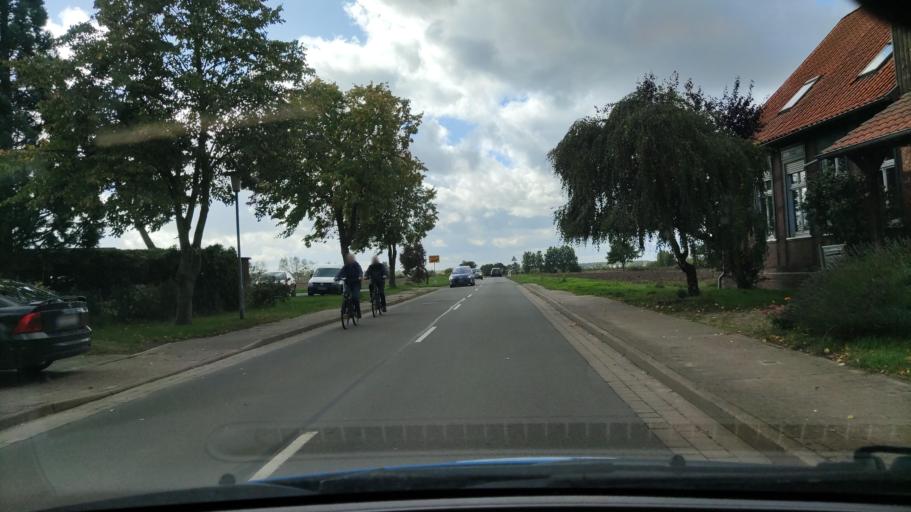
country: DE
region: Saxony-Anhalt
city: Salzwedel
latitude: 52.8550
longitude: 11.2077
